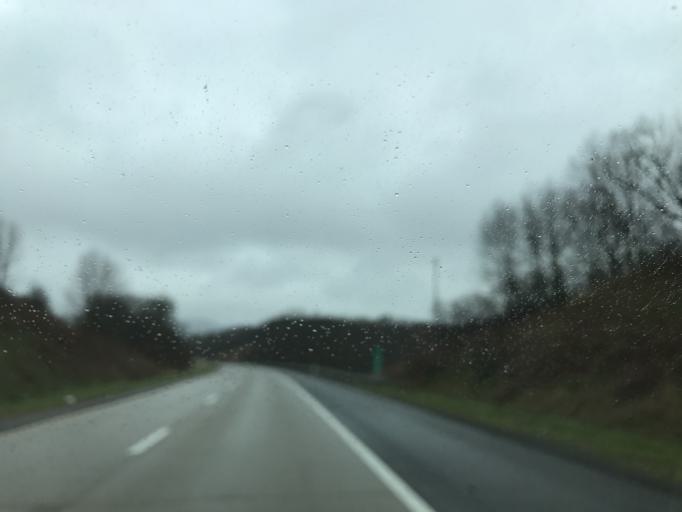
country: US
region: West Virginia
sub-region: Greenbrier County
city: Rainelle
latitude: 37.8883
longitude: -80.6659
